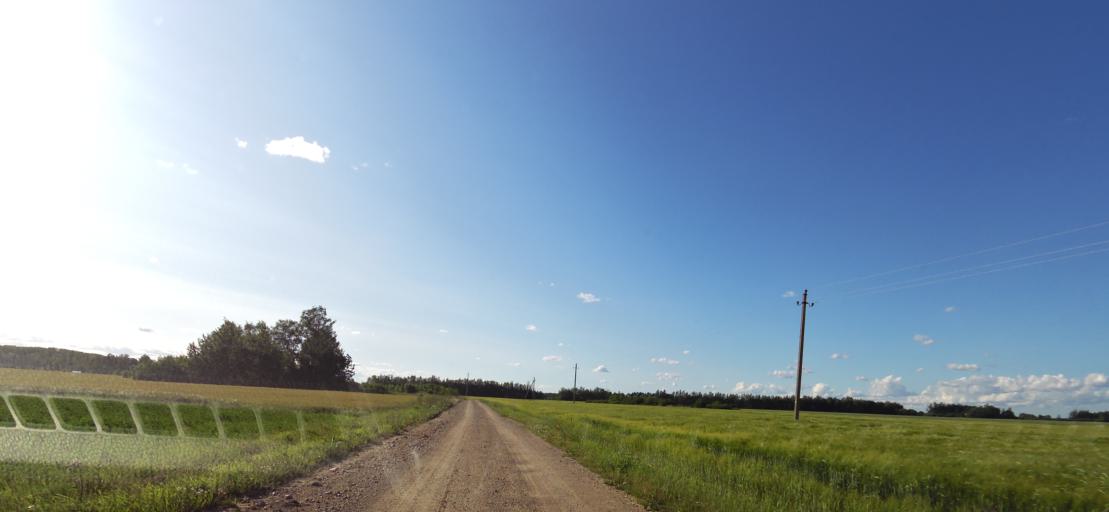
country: LT
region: Panevezys
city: Pasvalys
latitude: 56.1256
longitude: 24.5672
